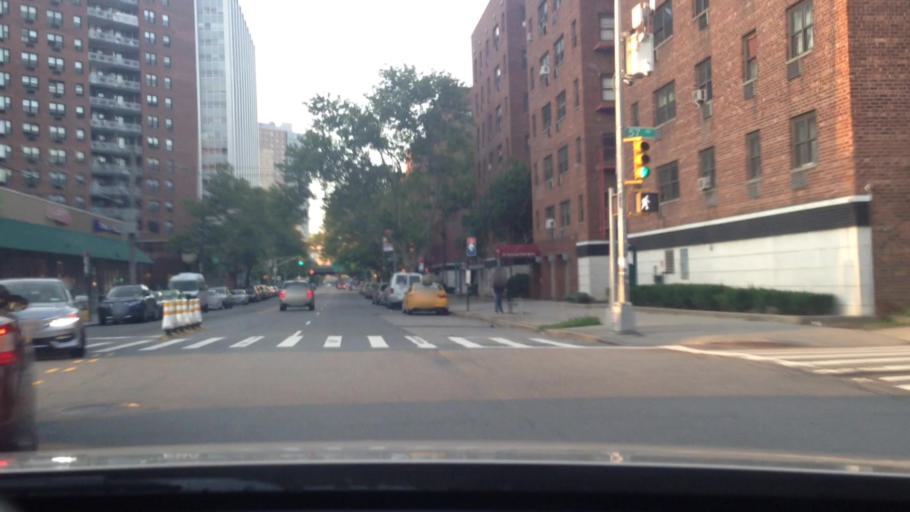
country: US
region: New York
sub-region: Queens County
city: Borough of Queens
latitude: 40.7367
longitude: -73.8659
